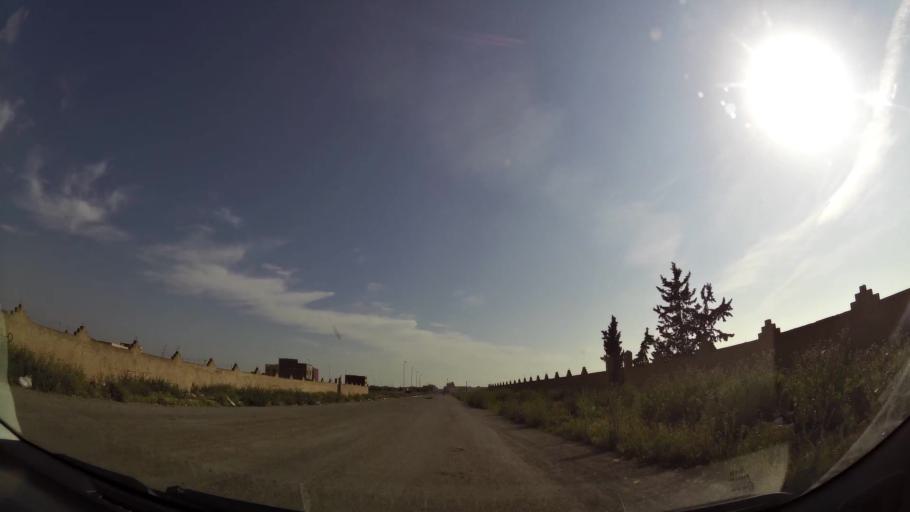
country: MA
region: Oriental
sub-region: Oujda-Angad
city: Oujda
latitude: 34.7218
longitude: -1.8872
